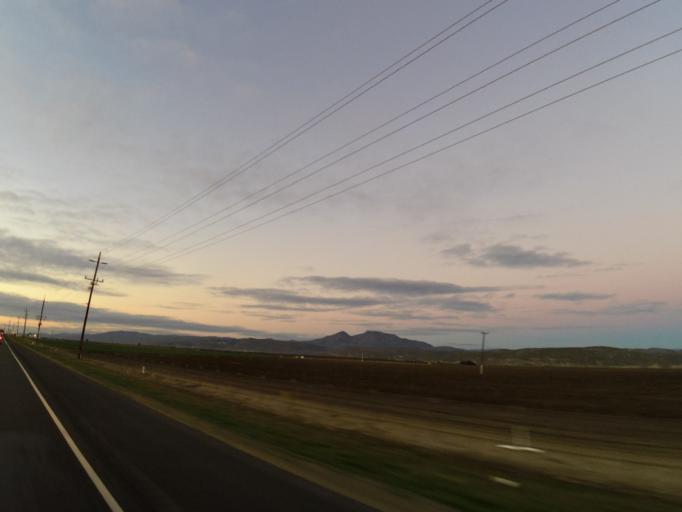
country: US
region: California
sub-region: Monterey County
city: Greenfield
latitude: 36.2885
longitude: -121.1953
